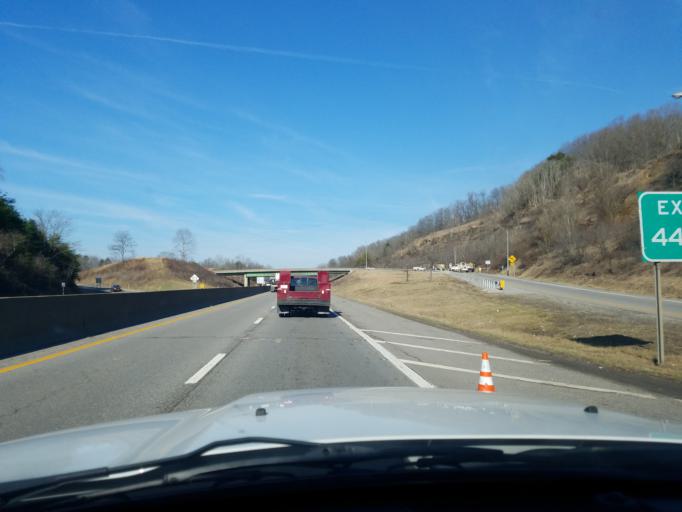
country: US
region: West Virginia
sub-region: Kanawha County
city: Nitro
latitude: 38.4472
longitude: -81.8469
